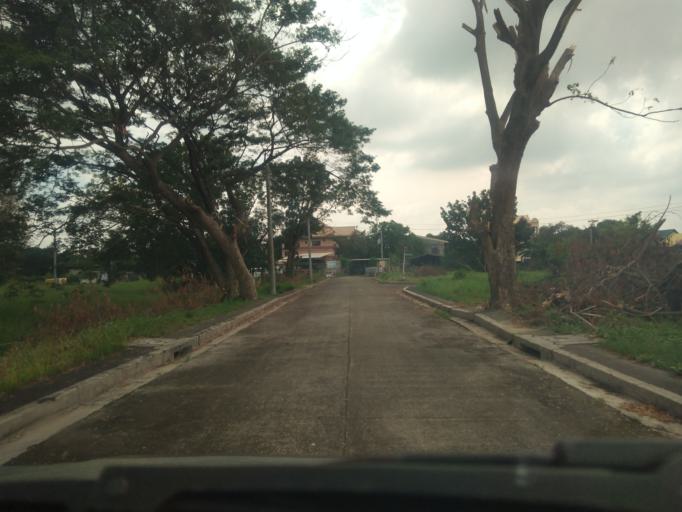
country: PH
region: Central Luzon
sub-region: Province of Pampanga
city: Santo Domingo
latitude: 15.0031
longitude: 120.7252
